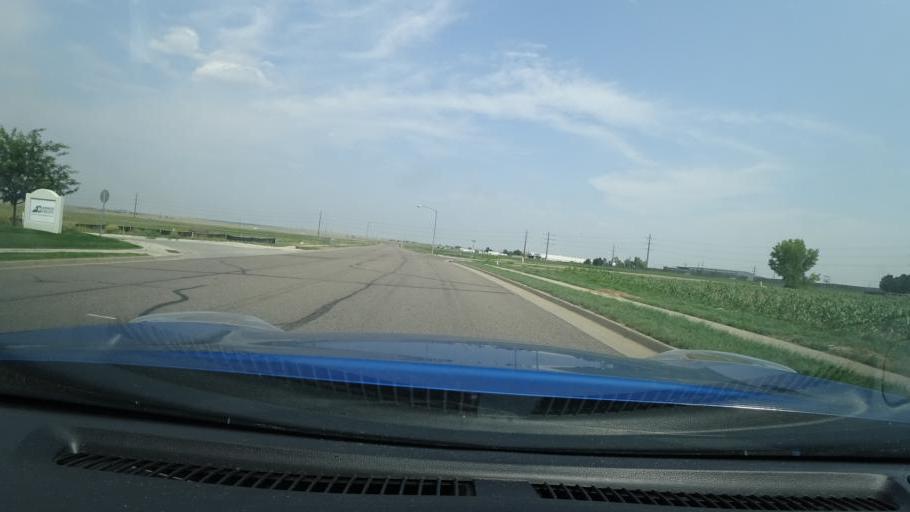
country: US
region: Colorado
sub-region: Adams County
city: Aurora
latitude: 39.7569
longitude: -104.7398
